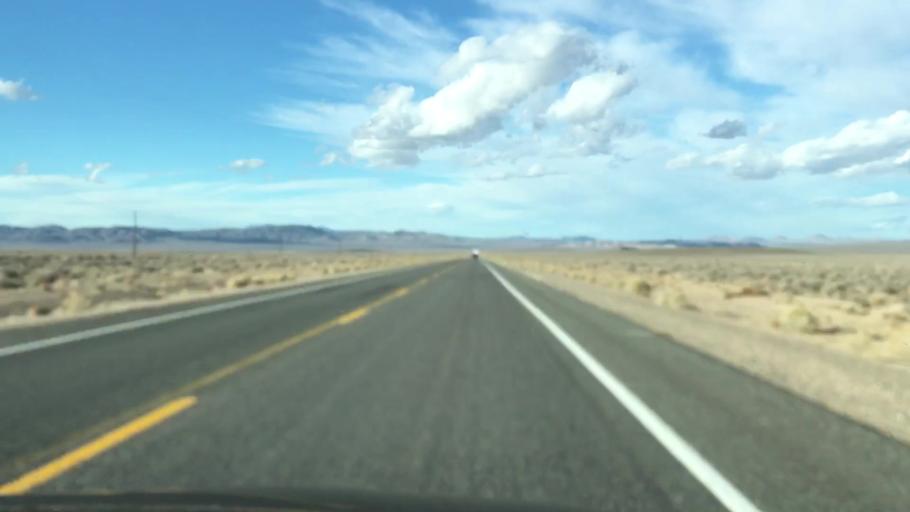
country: US
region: Nevada
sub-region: Esmeralda County
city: Goldfield
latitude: 37.4026
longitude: -117.1494
